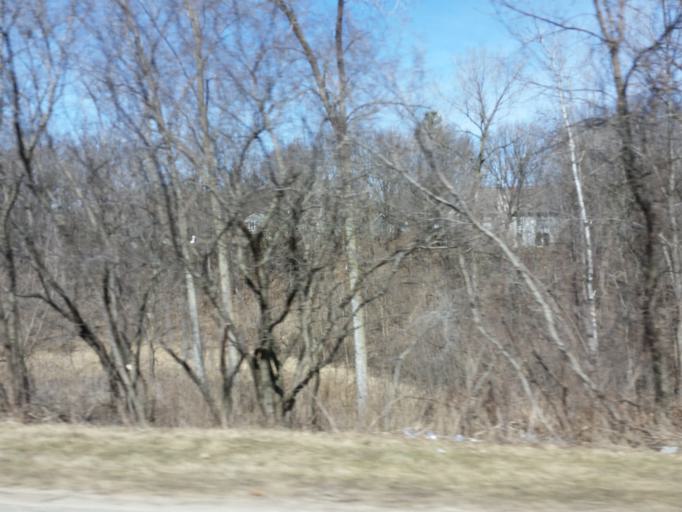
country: US
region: Minnesota
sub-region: Dakota County
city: Eagan
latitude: 44.7901
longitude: -93.1340
